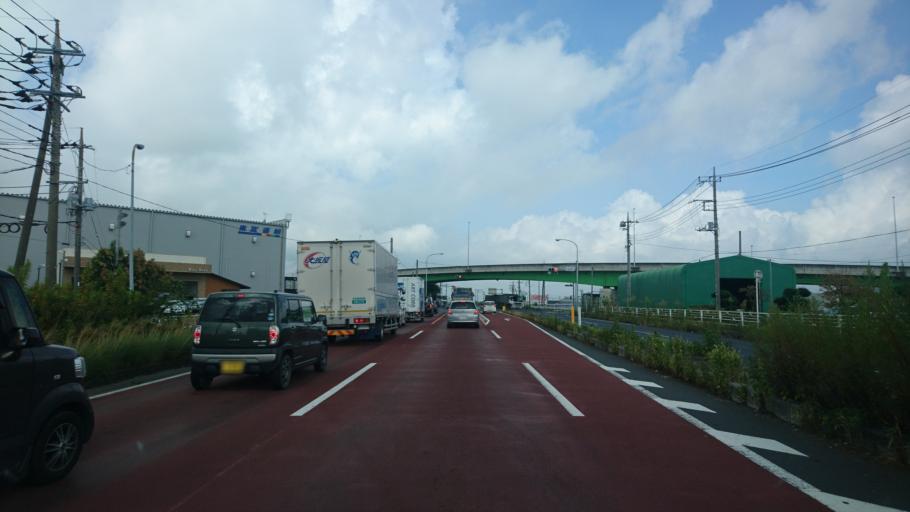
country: JP
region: Tochigi
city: Ashikaga
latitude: 36.2929
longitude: 139.4888
